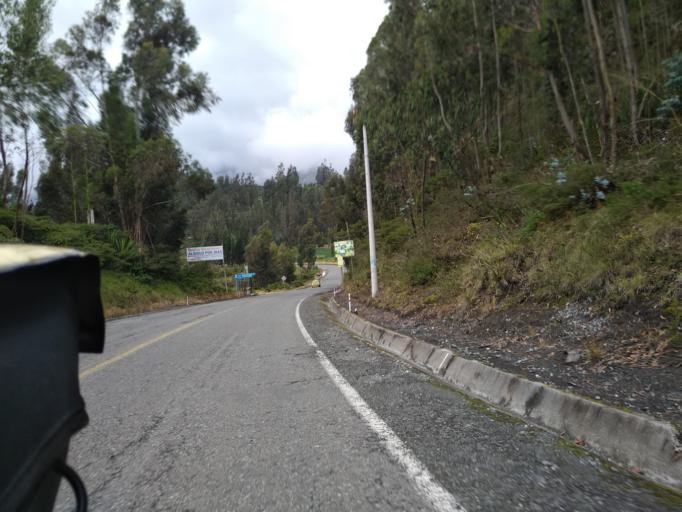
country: EC
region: Chimborazo
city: Guano
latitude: -1.5294
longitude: -78.5182
